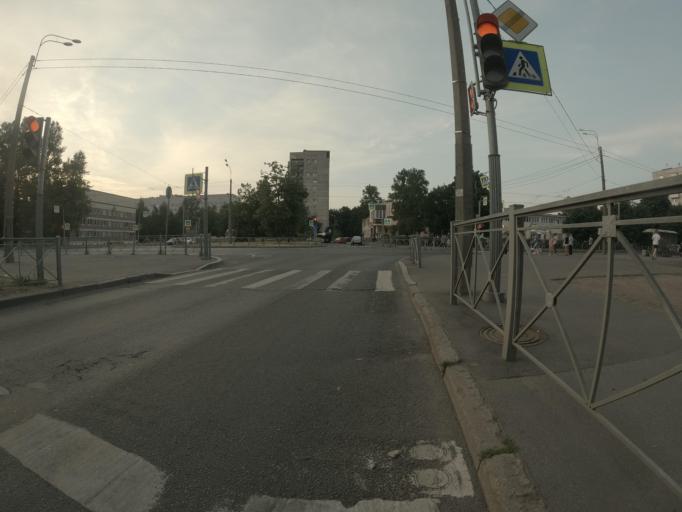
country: RU
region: Leningrad
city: Kalininskiy
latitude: 59.9851
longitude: 30.4120
